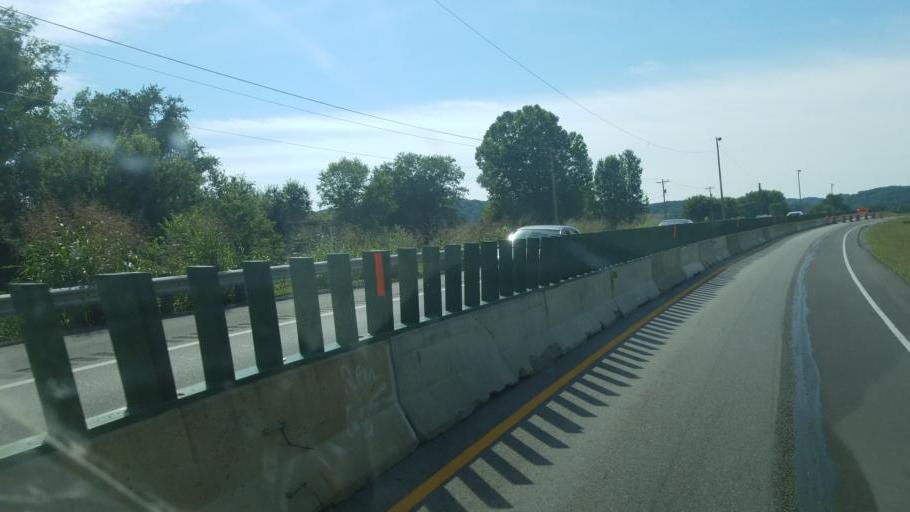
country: US
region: Ohio
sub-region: Athens County
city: Chauncey
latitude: 39.4058
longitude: -82.1791
